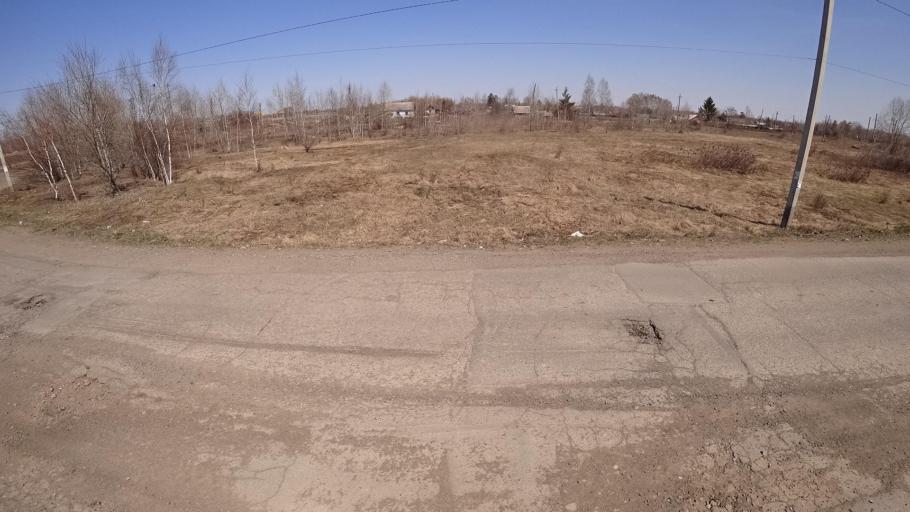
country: RU
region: Khabarovsk Krai
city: Khurba
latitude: 50.4107
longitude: 136.8824
